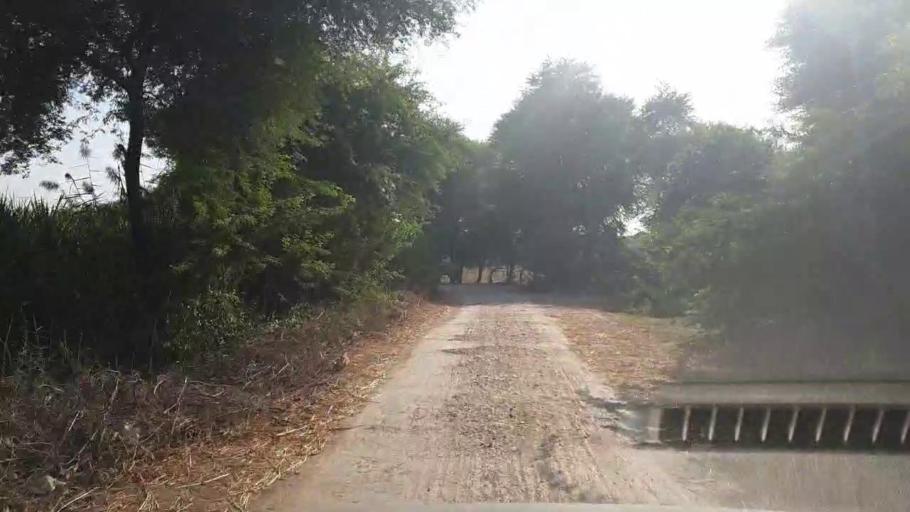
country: PK
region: Sindh
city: Matli
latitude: 25.0116
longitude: 68.7401
